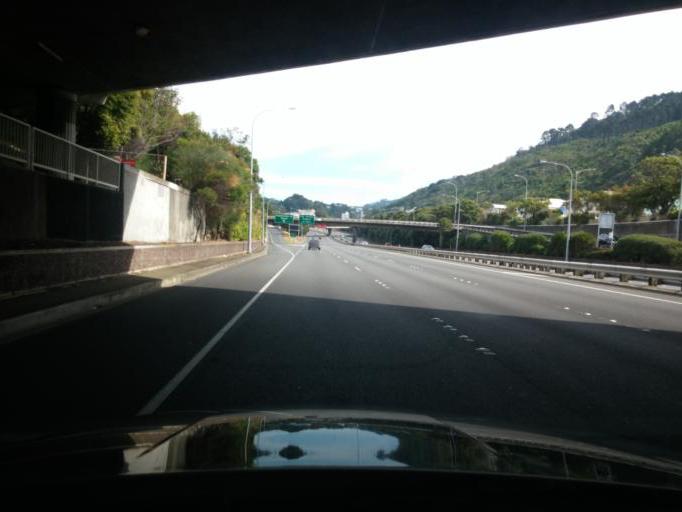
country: NZ
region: Wellington
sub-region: Wellington City
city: Wellington
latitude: -41.2721
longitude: 174.7780
